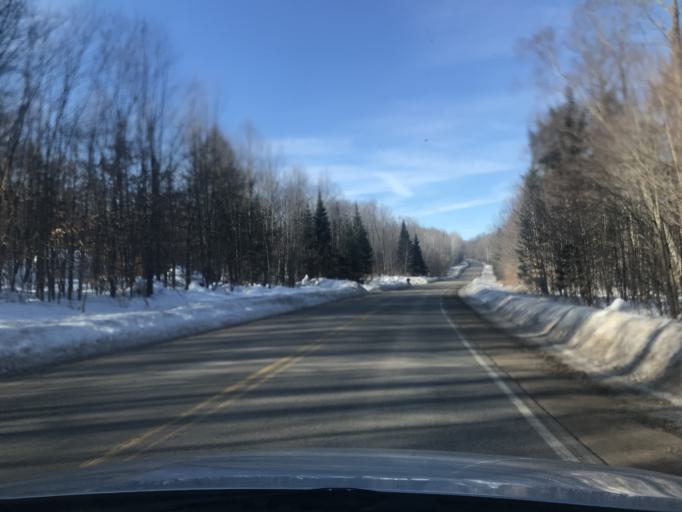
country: US
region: Michigan
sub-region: Dickinson County
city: Kingsford
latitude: 45.4186
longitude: -88.4025
